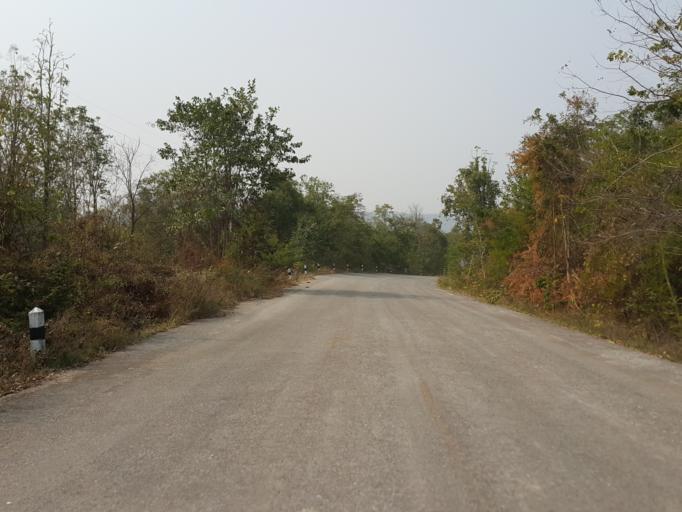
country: TH
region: Lampang
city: Mae Phrik
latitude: 17.4945
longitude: 99.0868
